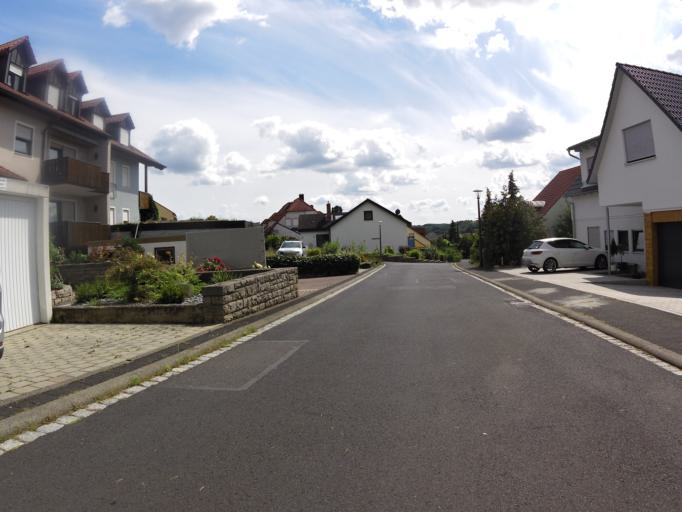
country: DE
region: Bavaria
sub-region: Regierungsbezirk Unterfranken
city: Sommerhausen
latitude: 49.7056
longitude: 10.0267
